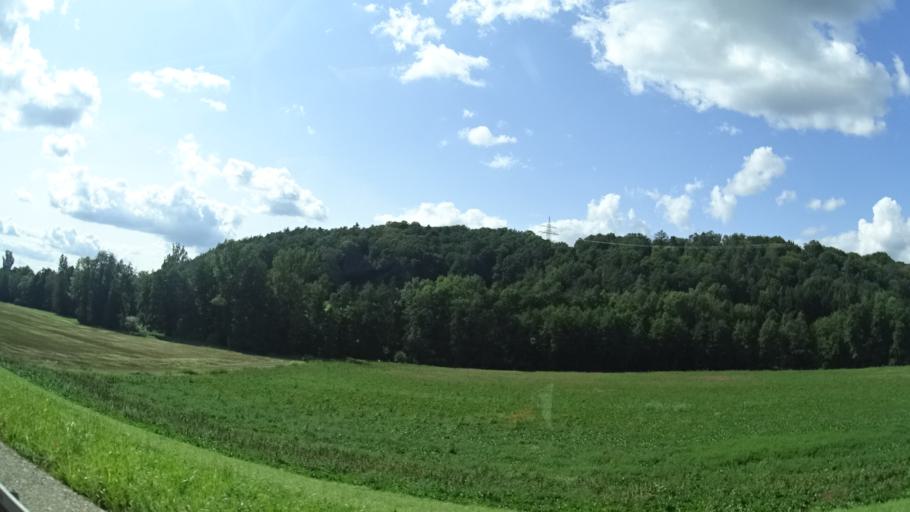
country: DE
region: Bavaria
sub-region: Regierungsbezirk Unterfranken
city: Ebelsbach
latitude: 49.9943
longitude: 10.6905
